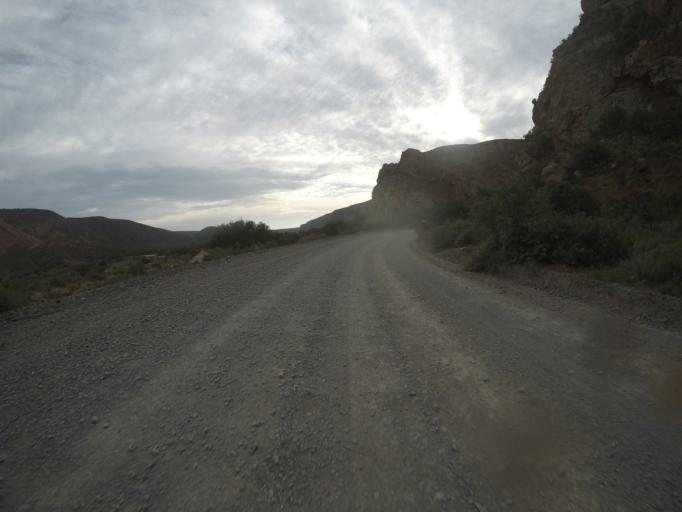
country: ZA
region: Eastern Cape
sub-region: Cacadu District Municipality
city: Willowmore
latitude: -33.5233
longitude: 23.6542
